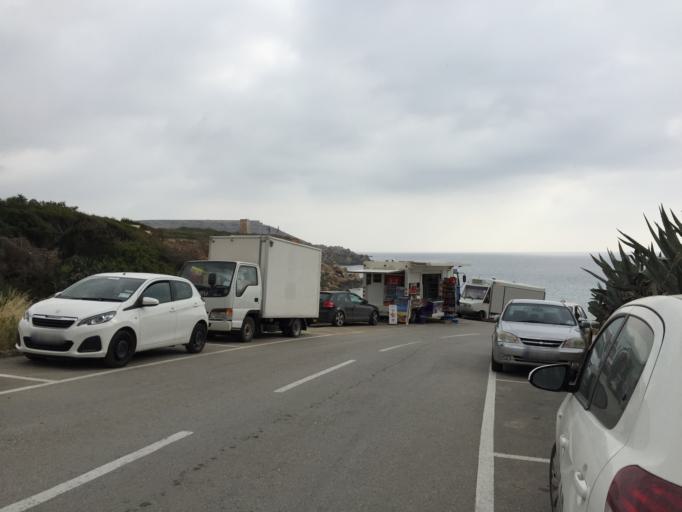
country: MT
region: L-Imgarr
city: Imgarr
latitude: 35.9344
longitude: 14.3456
